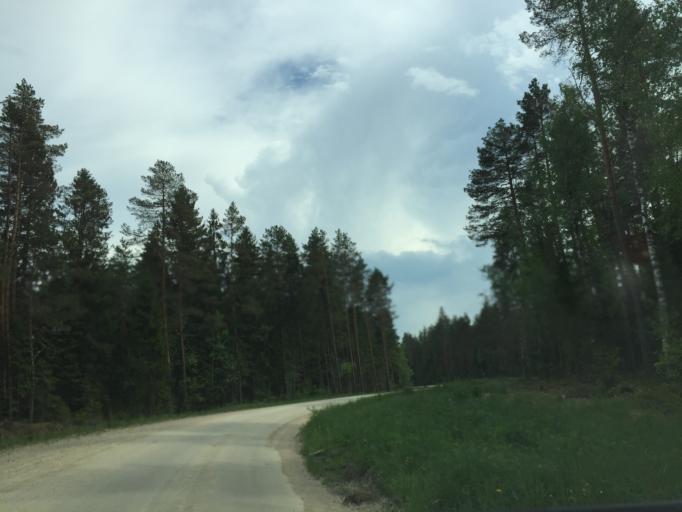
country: LV
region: Livani
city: Livani
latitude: 56.5621
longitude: 26.2217
